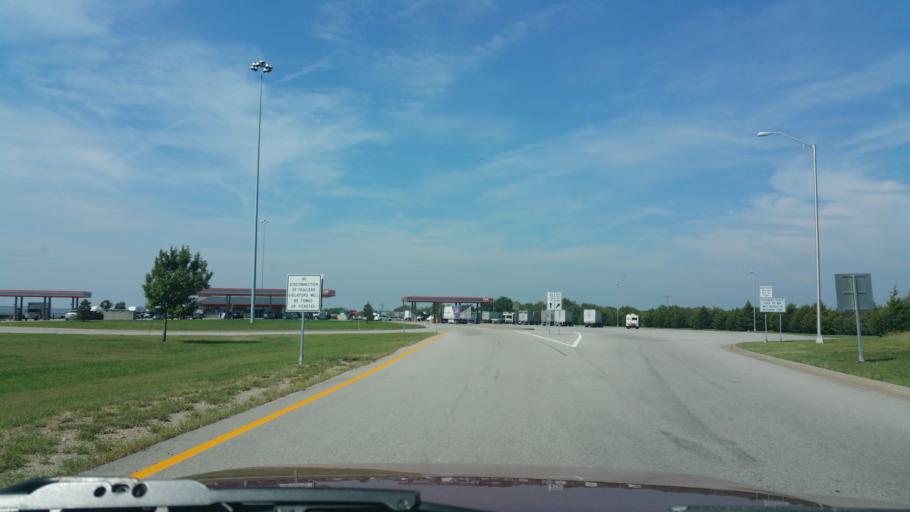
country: US
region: Kansas
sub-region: Shawnee County
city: Topeka
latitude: 39.0195
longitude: -95.5062
